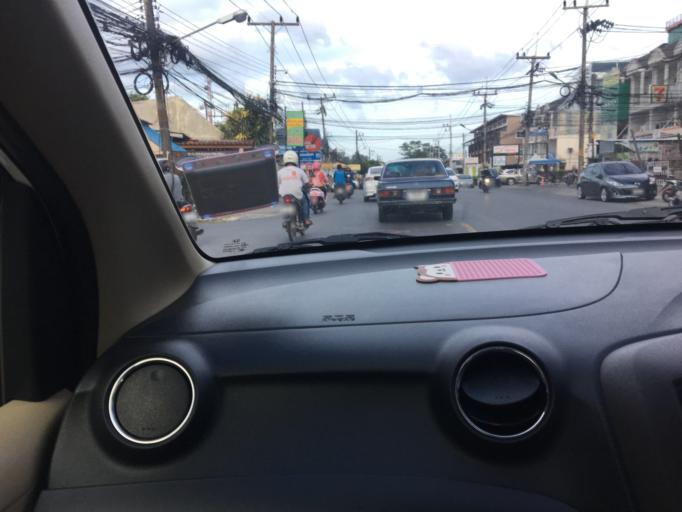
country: TH
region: Phuket
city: Ban Ratsada
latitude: 7.9080
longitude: 98.4012
